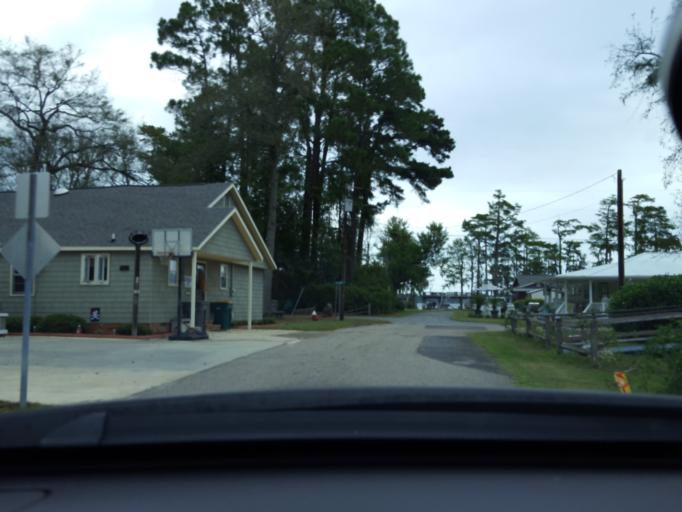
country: US
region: North Carolina
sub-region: Bladen County
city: Elizabethtown
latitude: 34.6394
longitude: -78.5102
